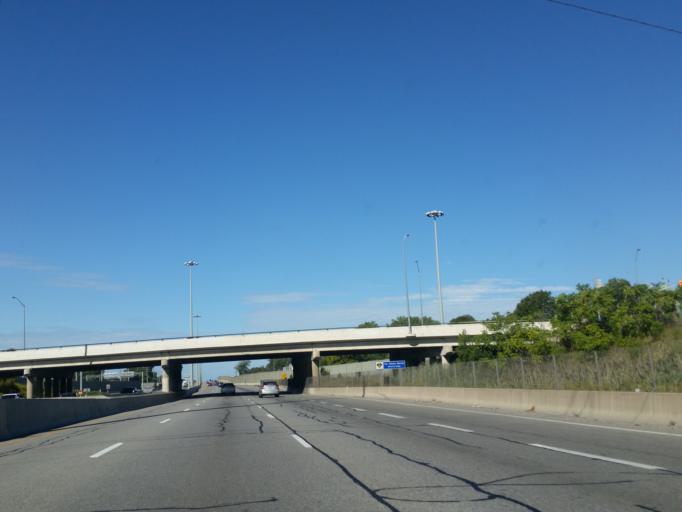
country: CA
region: Ontario
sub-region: Regional Municipality of Niagara
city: St. Catharines
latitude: 43.1731
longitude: -79.2301
